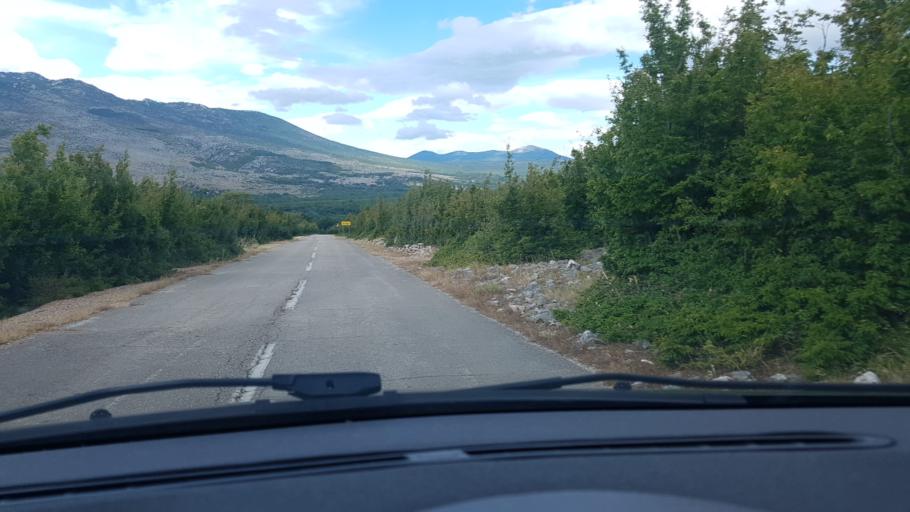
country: HR
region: Zadarska
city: Gracac
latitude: 44.1846
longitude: 15.8948
